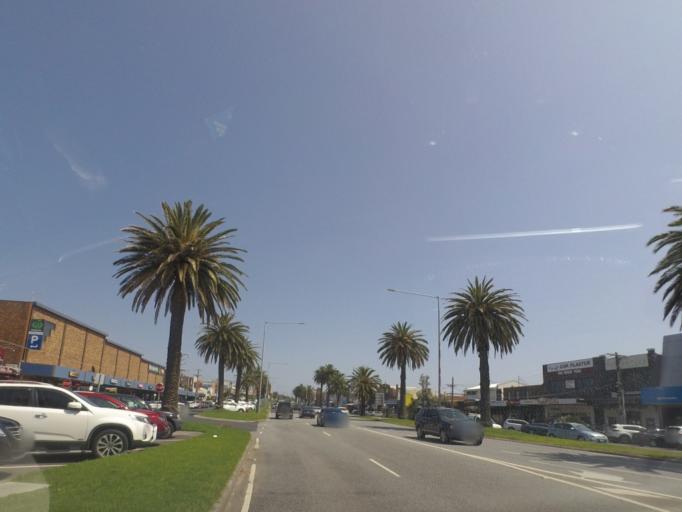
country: AU
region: Victoria
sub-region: Kingston
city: Mordialloc
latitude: -38.0083
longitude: 145.0876
